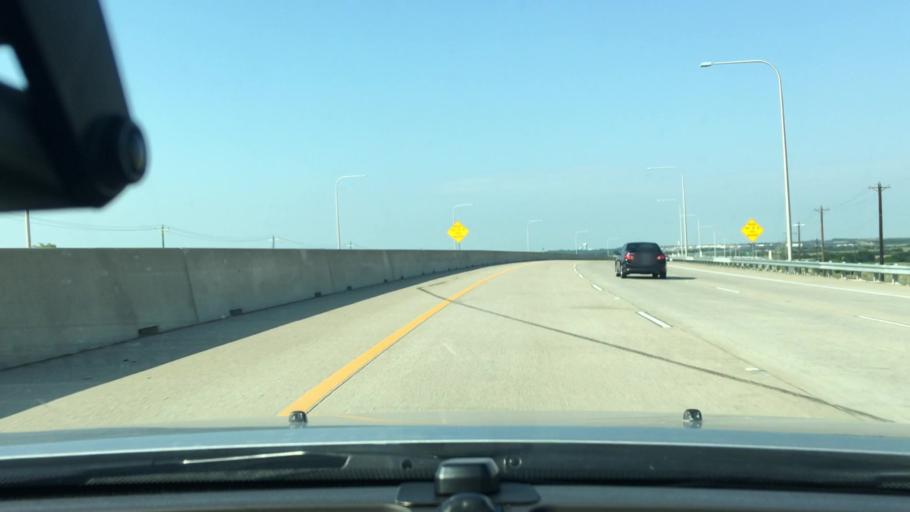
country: US
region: Texas
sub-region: Collin County
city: Frisco
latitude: 33.1949
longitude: -96.8368
